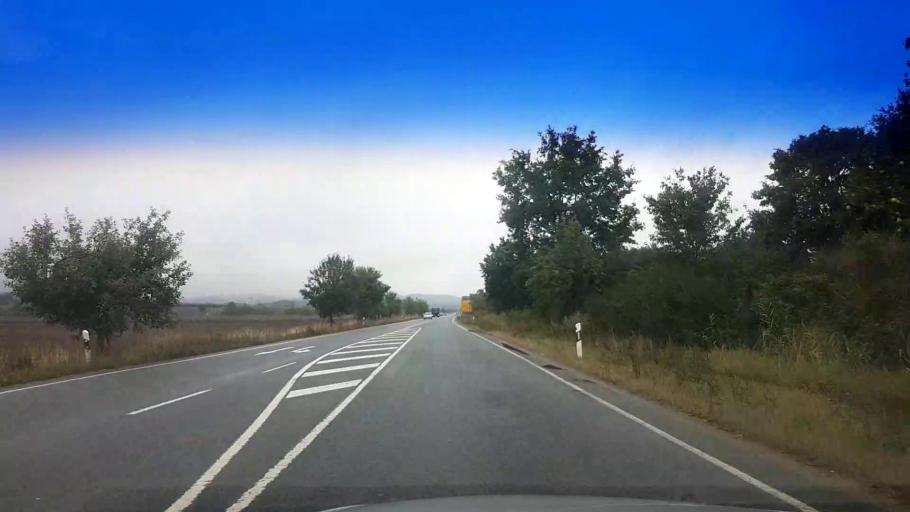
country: DE
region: Bavaria
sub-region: Upper Franconia
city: Eggolsheim
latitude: 49.7660
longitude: 11.0407
